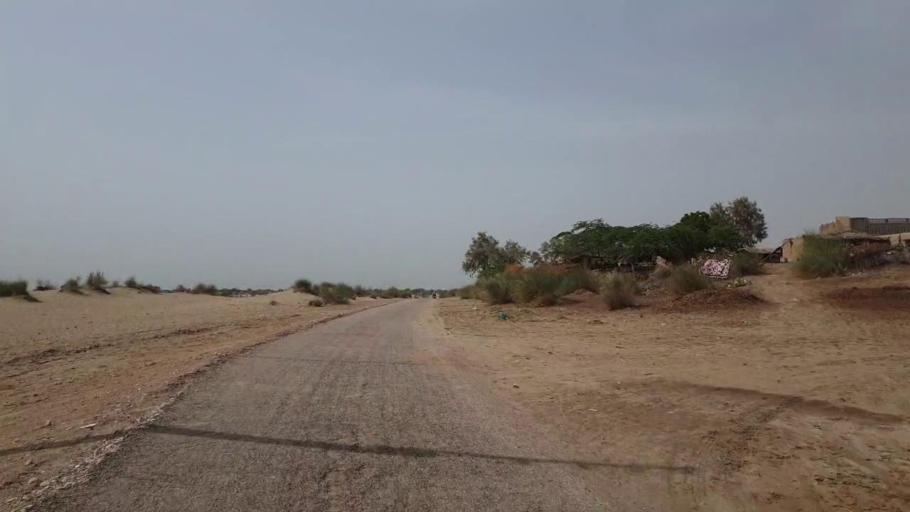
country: PK
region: Sindh
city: Bandhi
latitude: 26.5394
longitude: 68.3867
